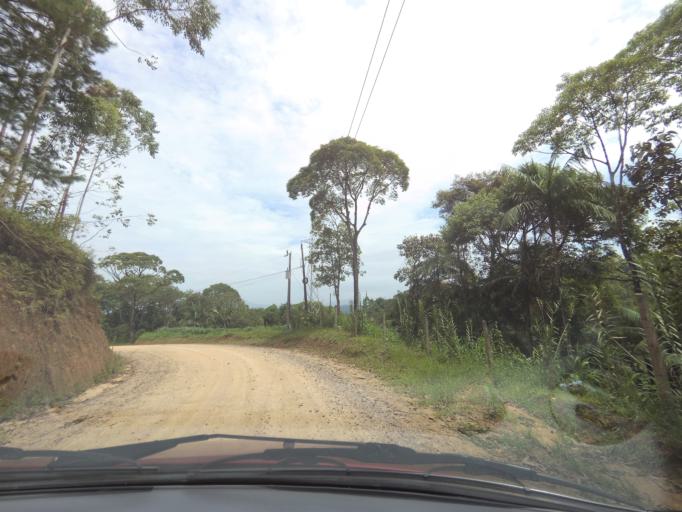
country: BR
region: Santa Catarina
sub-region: Brusque
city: Brusque
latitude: -27.0463
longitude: -49.0150
